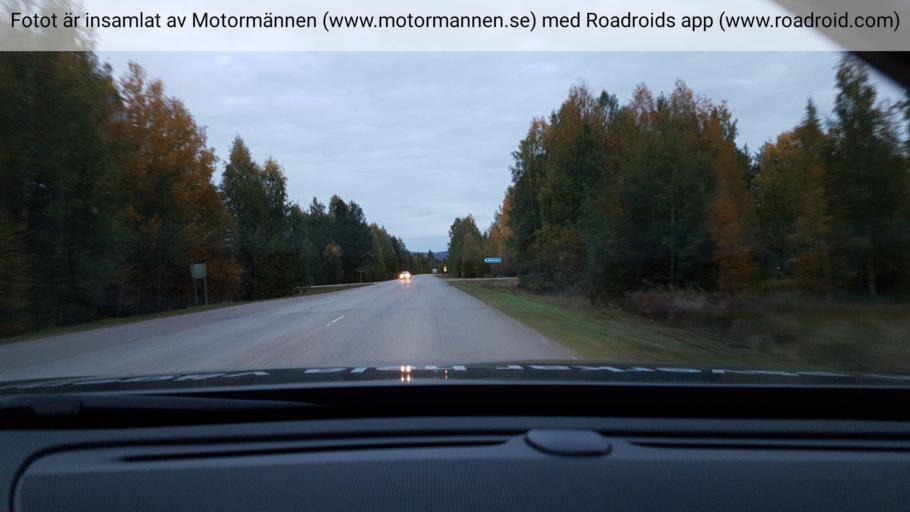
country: SE
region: Norrbotten
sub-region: Alvsbyns Kommun
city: AElvsbyn
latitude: 65.8456
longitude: 20.4793
